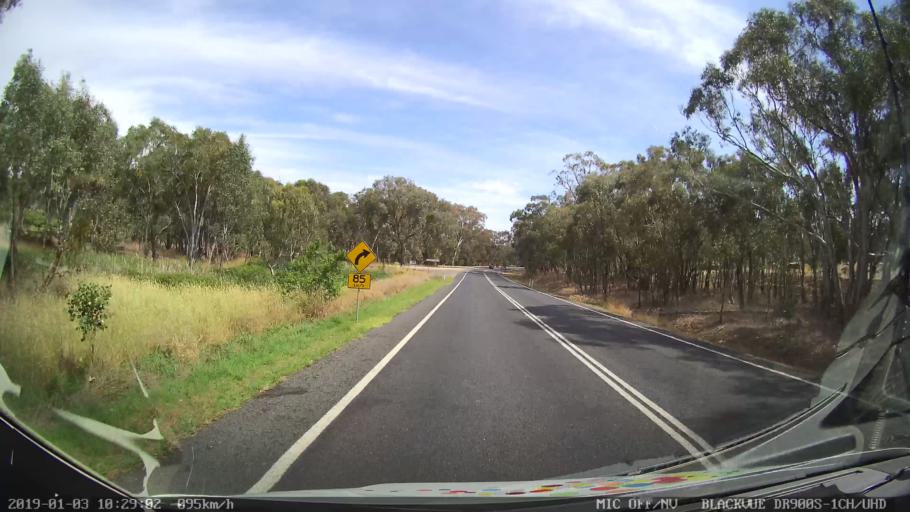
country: AU
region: New South Wales
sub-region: Young
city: Young
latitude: -34.3793
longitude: 148.2599
